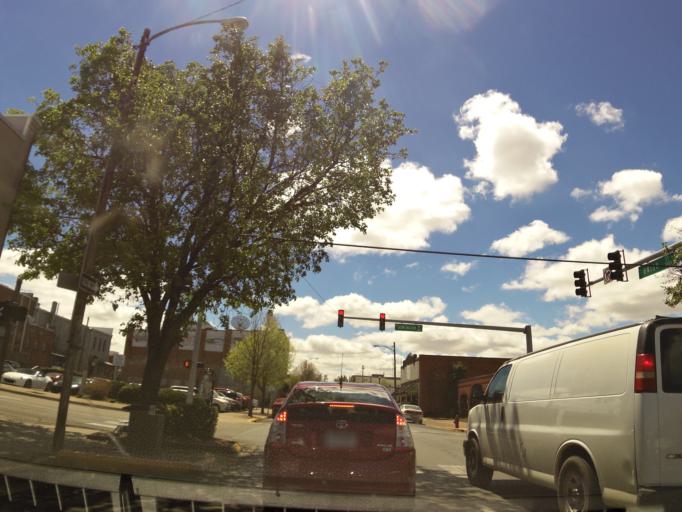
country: US
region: Arkansas
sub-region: Craighead County
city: Jonesboro
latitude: 35.8405
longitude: -90.7057
